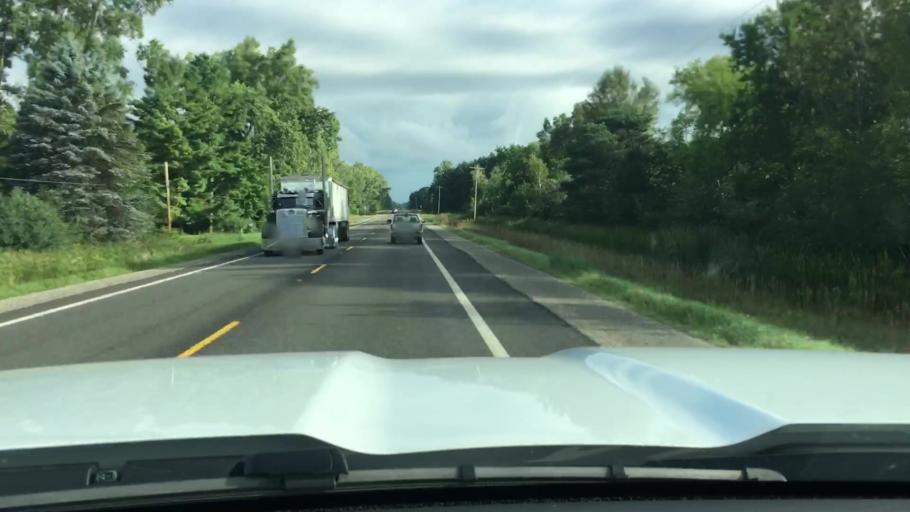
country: US
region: Michigan
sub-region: Tuscola County
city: Caro
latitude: 43.4209
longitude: -83.3844
